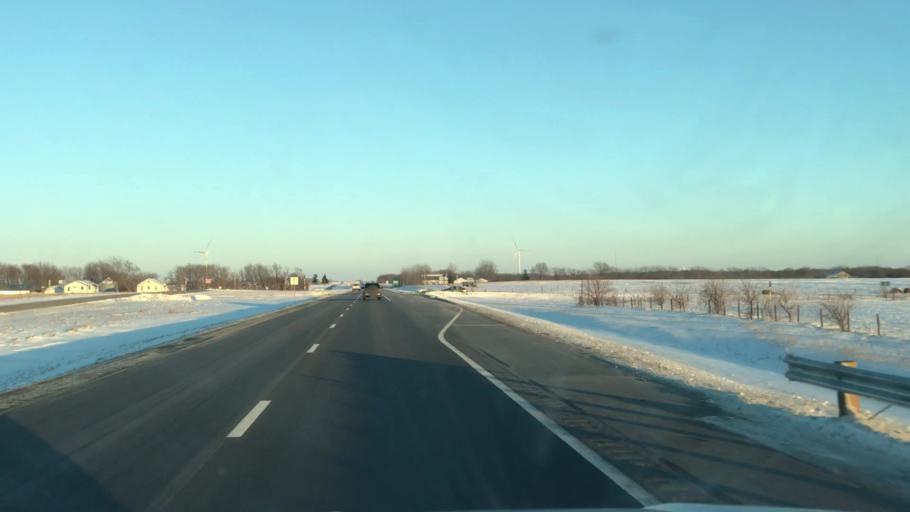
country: US
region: Missouri
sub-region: DeKalb County
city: Maysville
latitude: 39.7615
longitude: -94.4034
